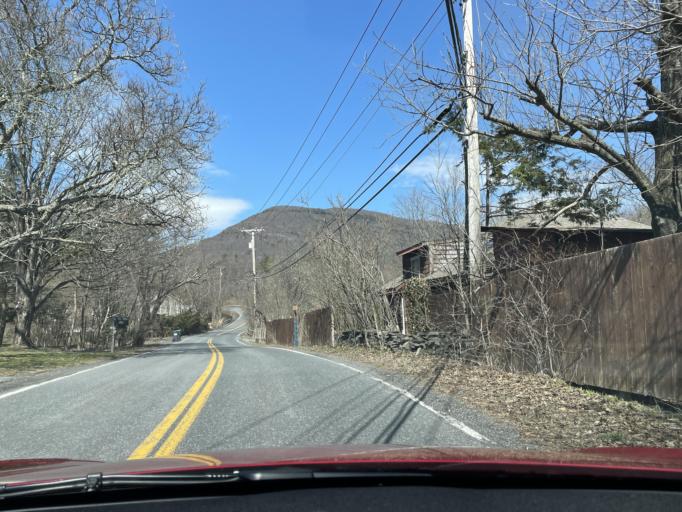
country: US
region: New York
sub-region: Ulster County
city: Manorville
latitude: 42.1118
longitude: -74.0463
